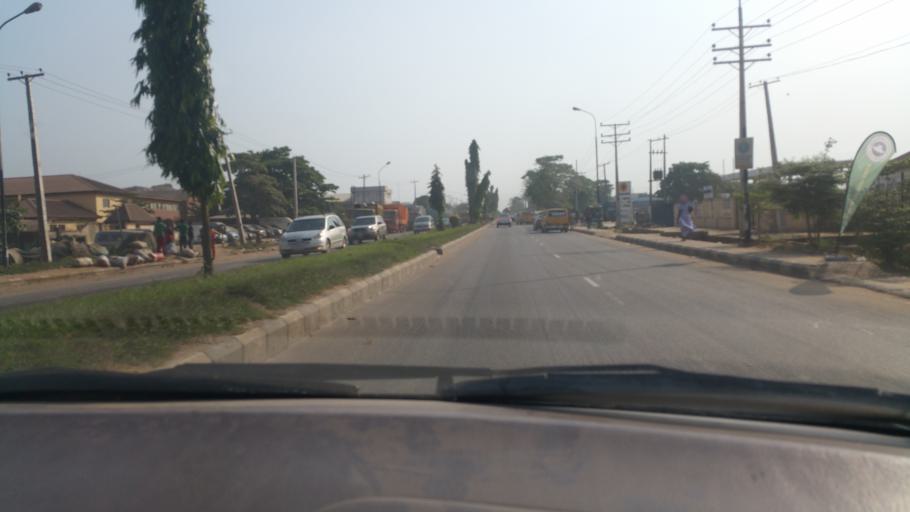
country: NG
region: Lagos
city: Ikotun
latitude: 6.5667
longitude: 3.2514
